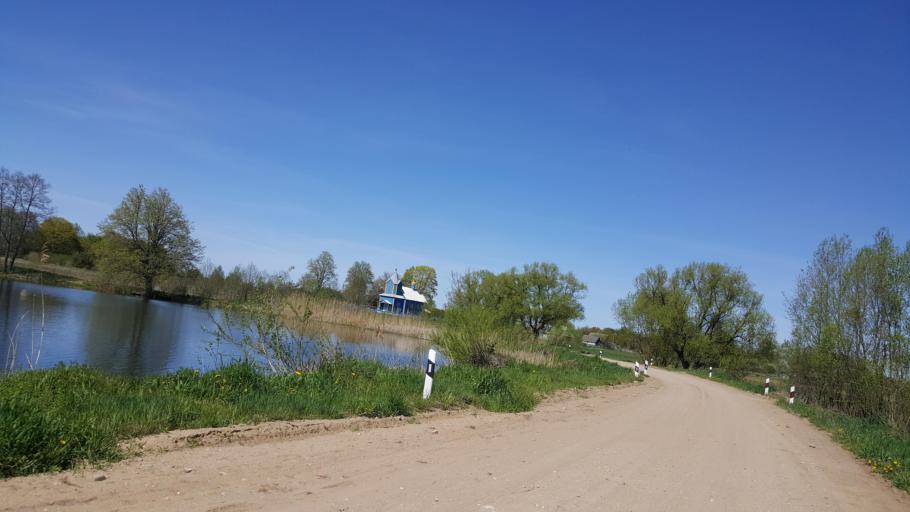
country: BY
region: Brest
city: Kamyanyets
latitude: 52.4525
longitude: 23.8736
